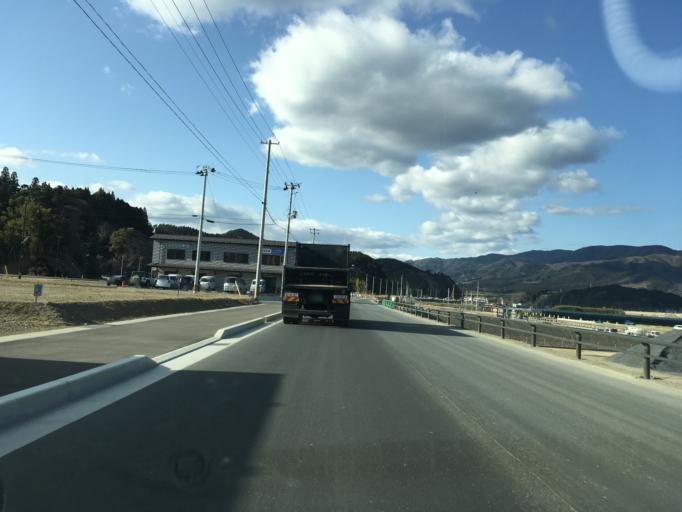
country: JP
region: Iwate
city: Ofunato
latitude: 39.0067
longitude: 141.6169
